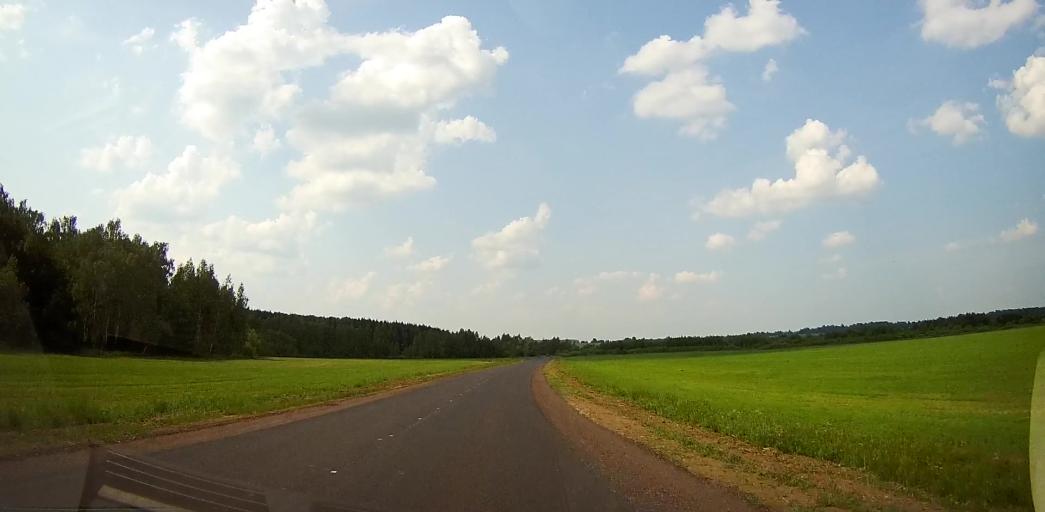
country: RU
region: Moskovskaya
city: Malino
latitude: 55.0591
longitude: 38.1402
